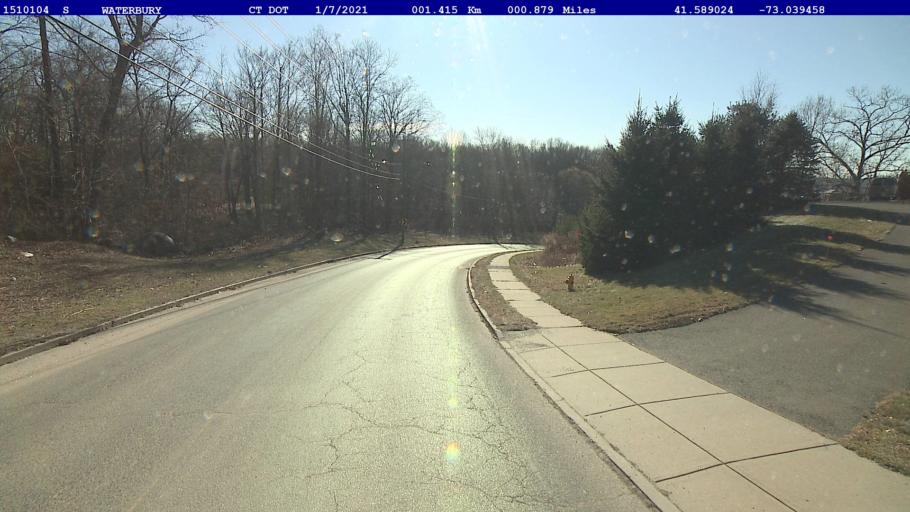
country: US
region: Connecticut
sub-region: New Haven County
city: Waterbury
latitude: 41.5890
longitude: -73.0395
